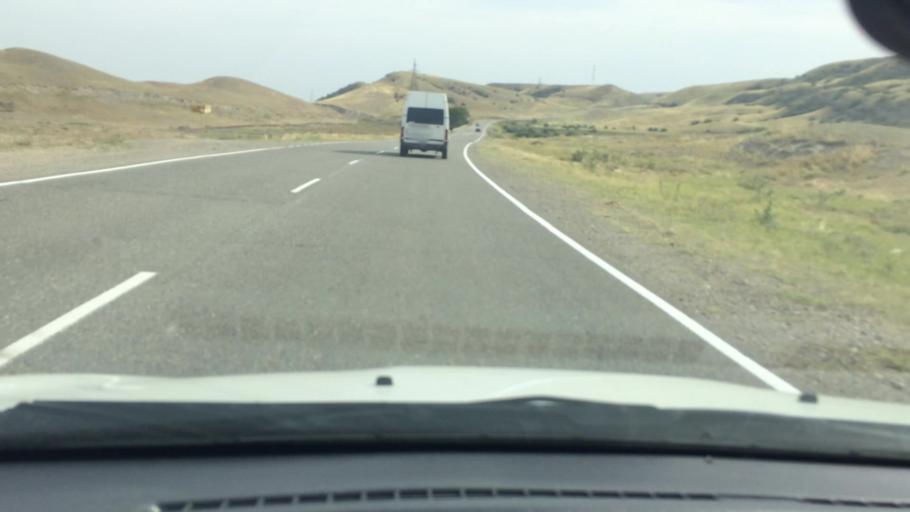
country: GE
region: Kvemo Kartli
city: Rust'avi
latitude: 41.5316
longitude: 44.9841
